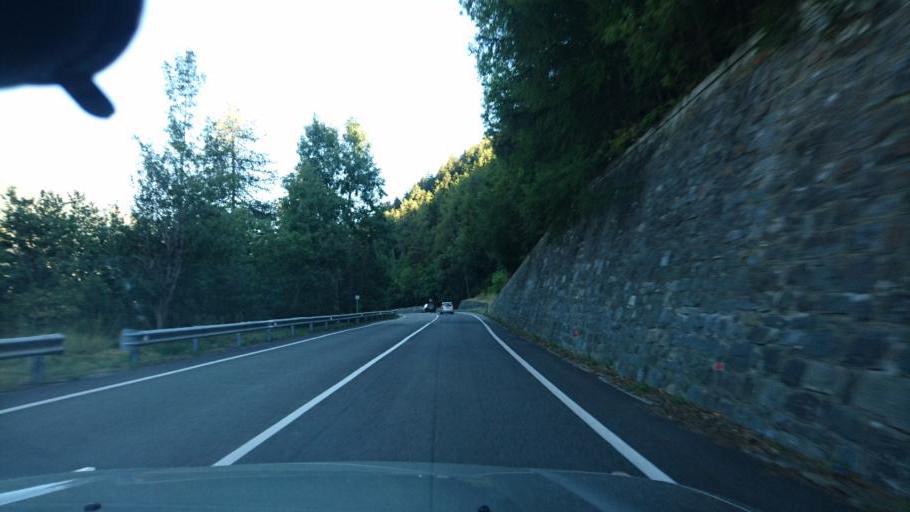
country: IT
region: Aosta Valley
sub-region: Valle d'Aosta
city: Allein
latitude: 45.7998
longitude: 7.2741
